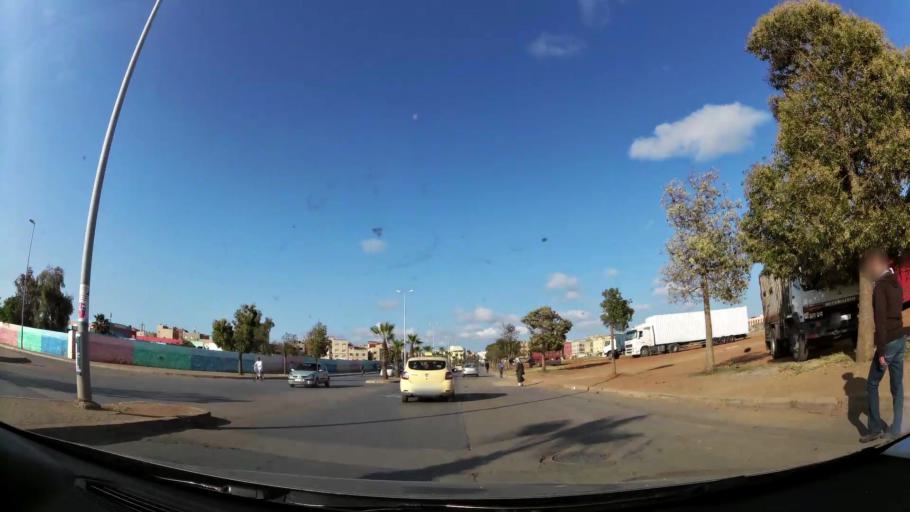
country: MA
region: Rabat-Sale-Zemmour-Zaer
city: Sale
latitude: 34.0562
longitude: -6.7913
